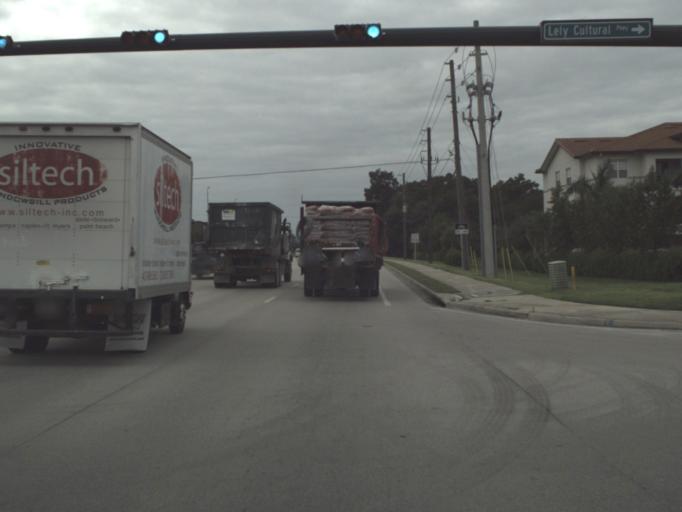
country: US
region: Florida
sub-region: Collier County
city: Lely Resort
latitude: 26.1041
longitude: -81.6874
